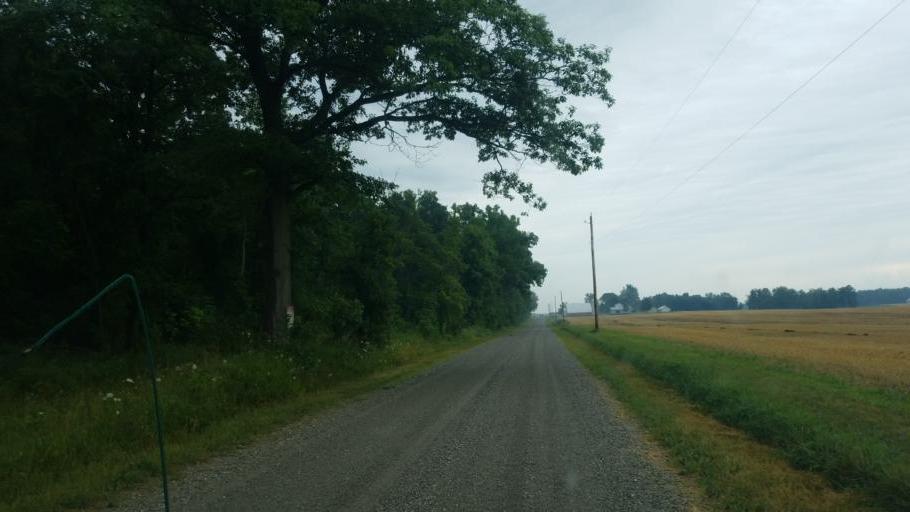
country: US
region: Indiana
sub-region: DeKalb County
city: Butler
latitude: 41.4555
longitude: -84.9099
